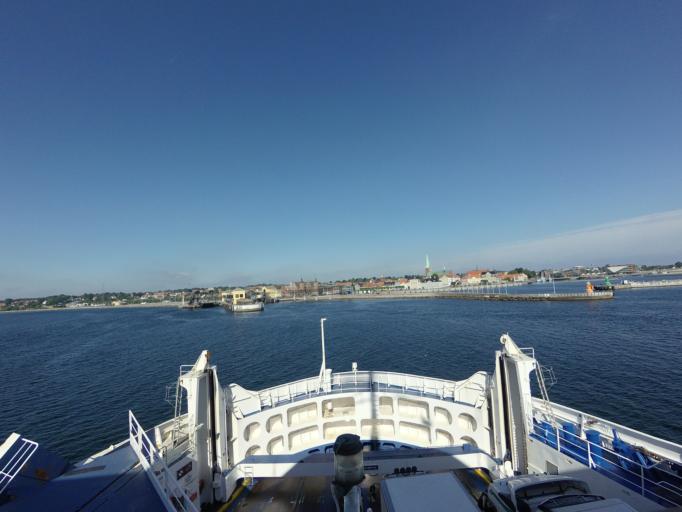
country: DK
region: Capital Region
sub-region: Helsingor Kommune
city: Helsingor
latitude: 56.0332
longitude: 12.6215
